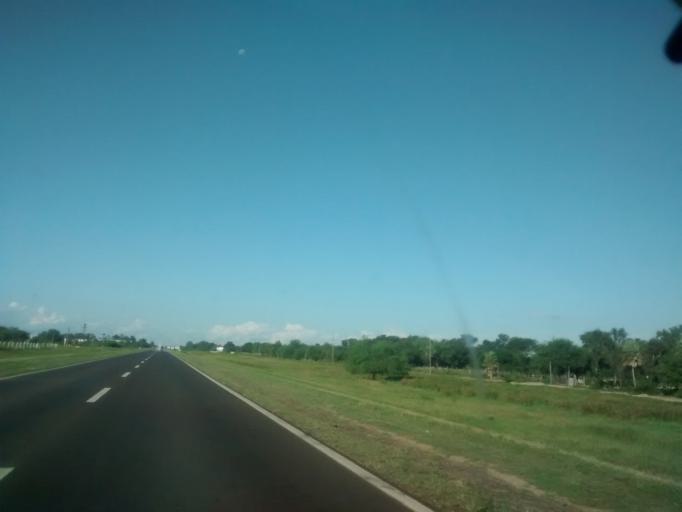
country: AR
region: Chaco
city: Fontana
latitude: -27.4784
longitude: -59.0595
